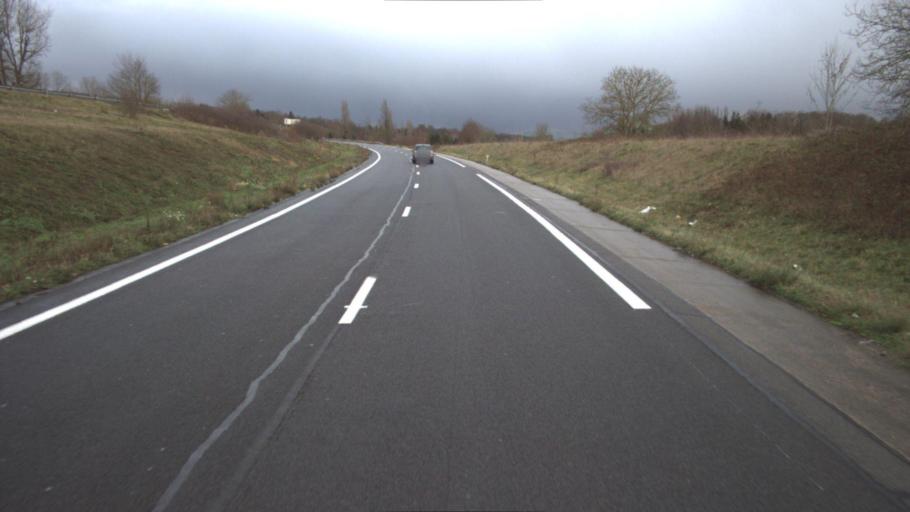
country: FR
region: Ile-de-France
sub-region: Departement de Seine-et-Marne
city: Cely
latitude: 48.4740
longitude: 2.5172
